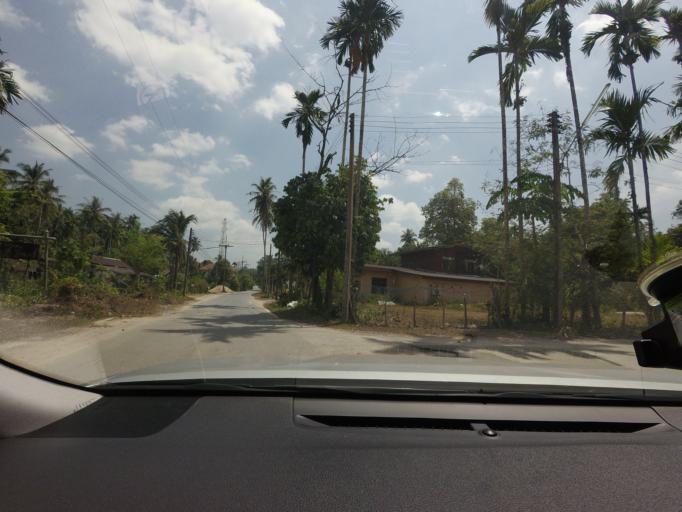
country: TH
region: Narathiwat
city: Rueso
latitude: 6.3891
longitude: 101.5092
